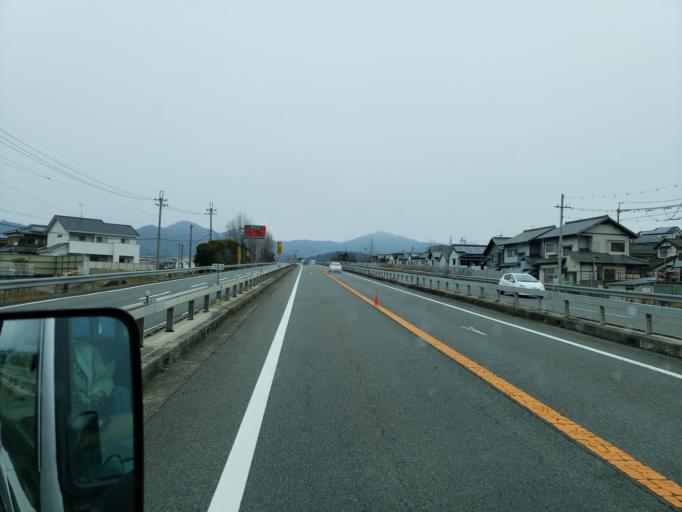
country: JP
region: Hyogo
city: Himeji
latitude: 34.9497
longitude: 134.7666
